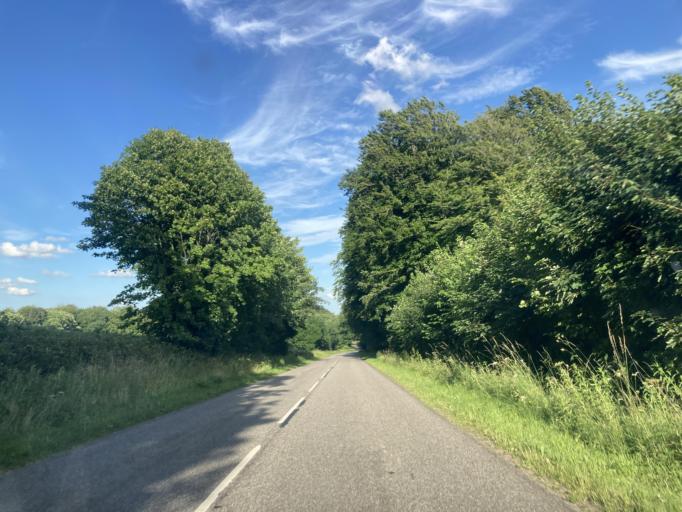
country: DK
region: South Denmark
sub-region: Kolding Kommune
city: Lunderskov
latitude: 55.4836
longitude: 9.3773
